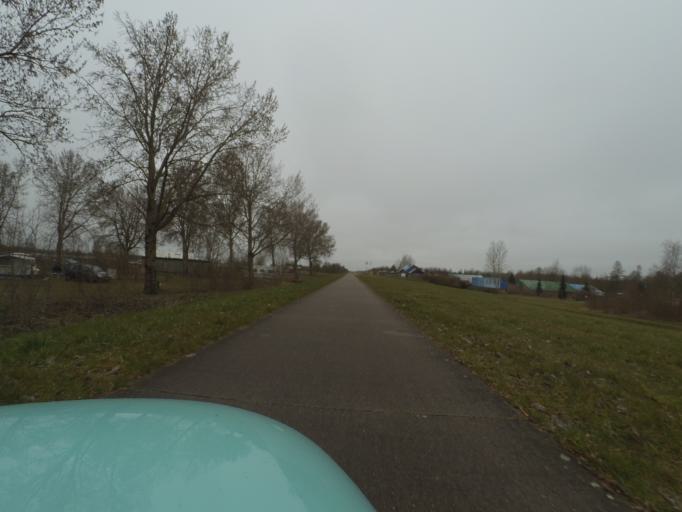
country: NL
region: Flevoland
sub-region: Gemeente Zeewolde
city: Zeewolde
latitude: 52.3129
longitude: 5.5463
